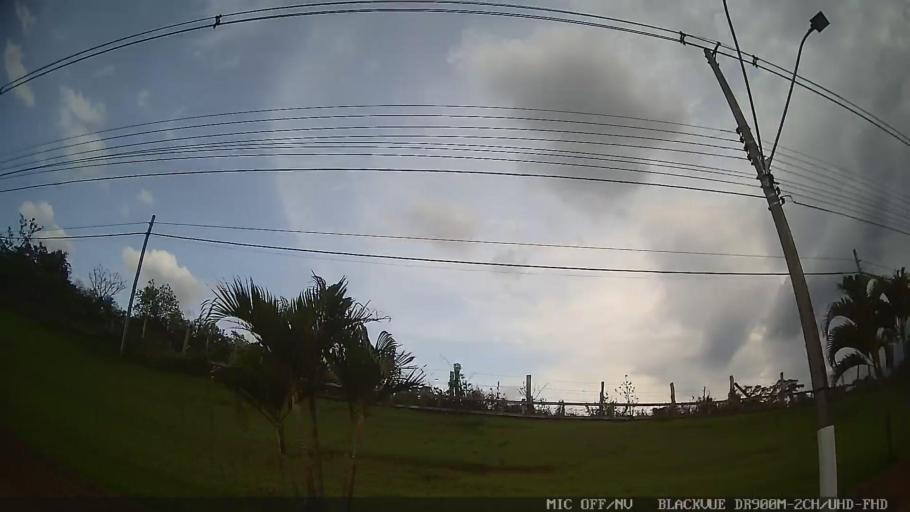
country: BR
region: Sao Paulo
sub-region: Itatiba
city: Itatiba
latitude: -22.8867
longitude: -46.7913
